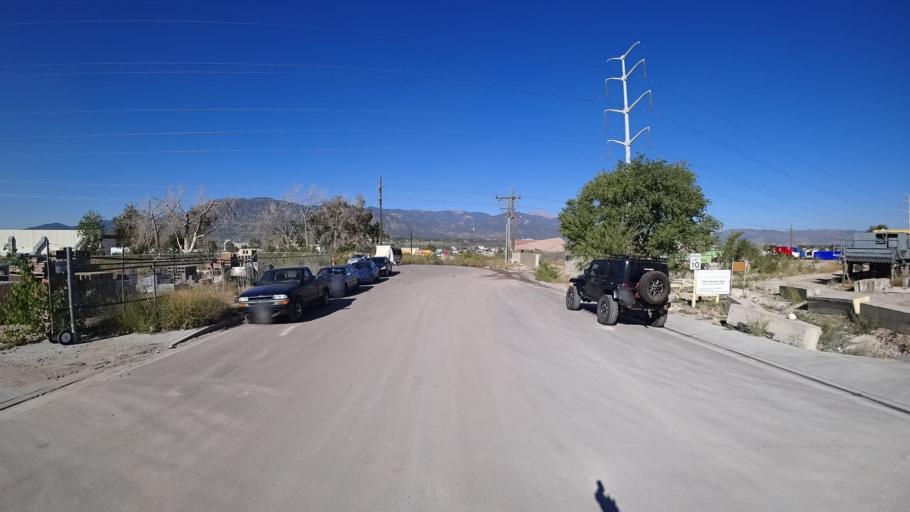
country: US
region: Colorado
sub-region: El Paso County
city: Stratmoor
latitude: 38.7817
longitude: -104.7692
